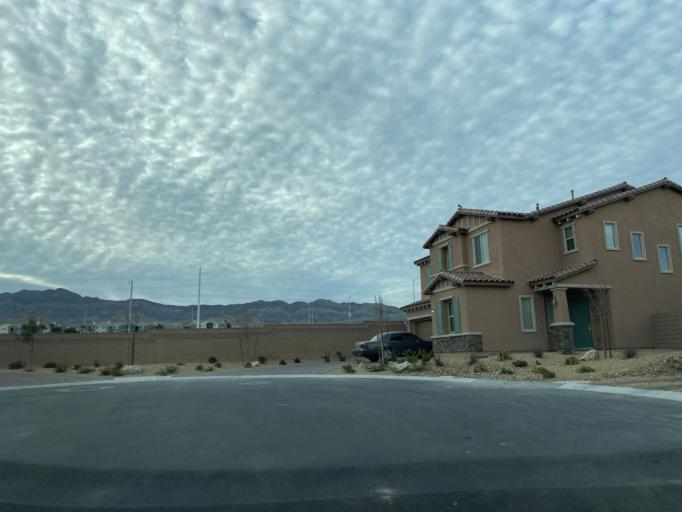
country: US
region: Nevada
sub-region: Clark County
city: Summerlin South
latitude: 36.2767
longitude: -115.3250
